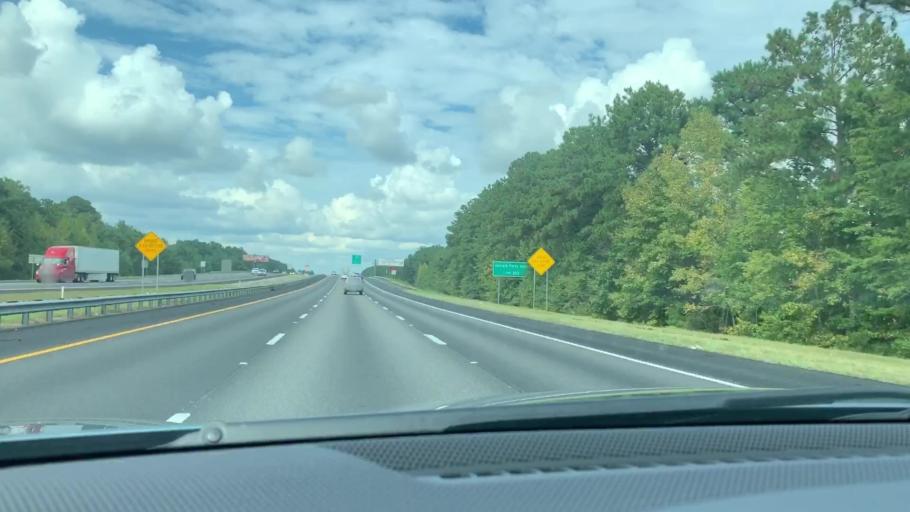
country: US
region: Georgia
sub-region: Chatham County
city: Pooler
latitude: 32.0977
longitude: -81.2364
